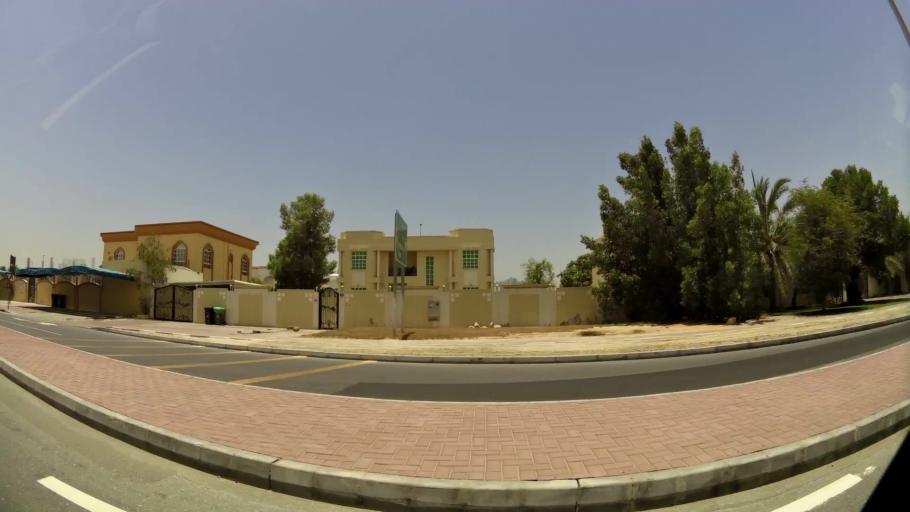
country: AE
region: Dubai
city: Dubai
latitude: 25.0921
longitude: 55.1893
